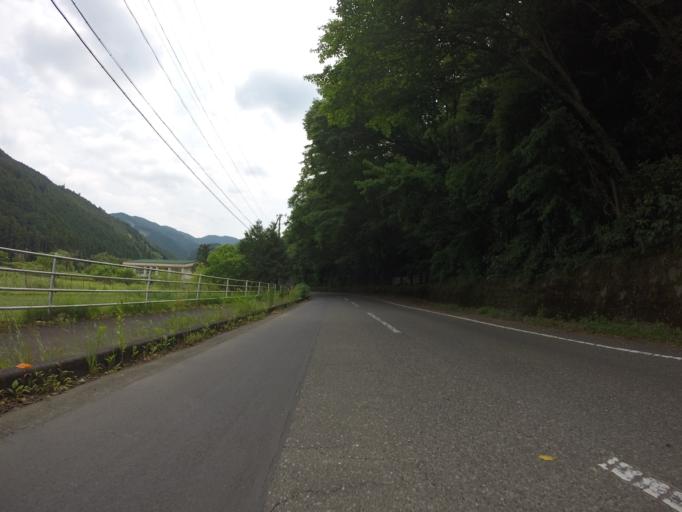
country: JP
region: Shizuoka
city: Shizuoka-shi
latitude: 35.1179
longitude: 138.3270
